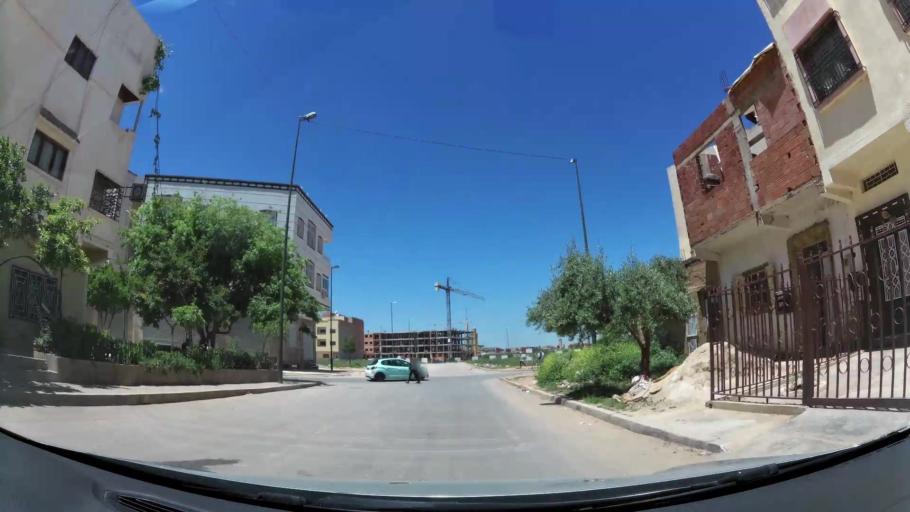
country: MA
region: Meknes-Tafilalet
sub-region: Meknes
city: Meknes
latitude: 33.8674
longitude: -5.5663
